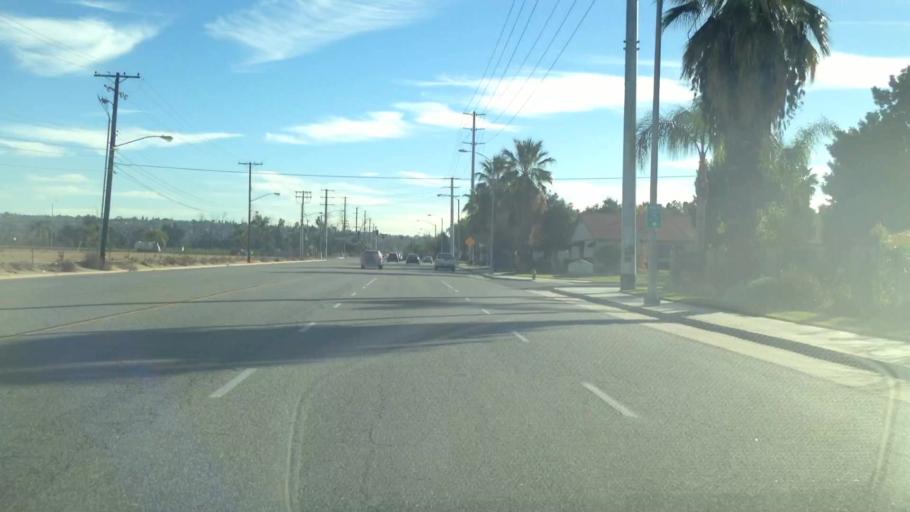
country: US
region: California
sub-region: Riverside County
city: Highgrove
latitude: 33.9705
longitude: -117.3486
